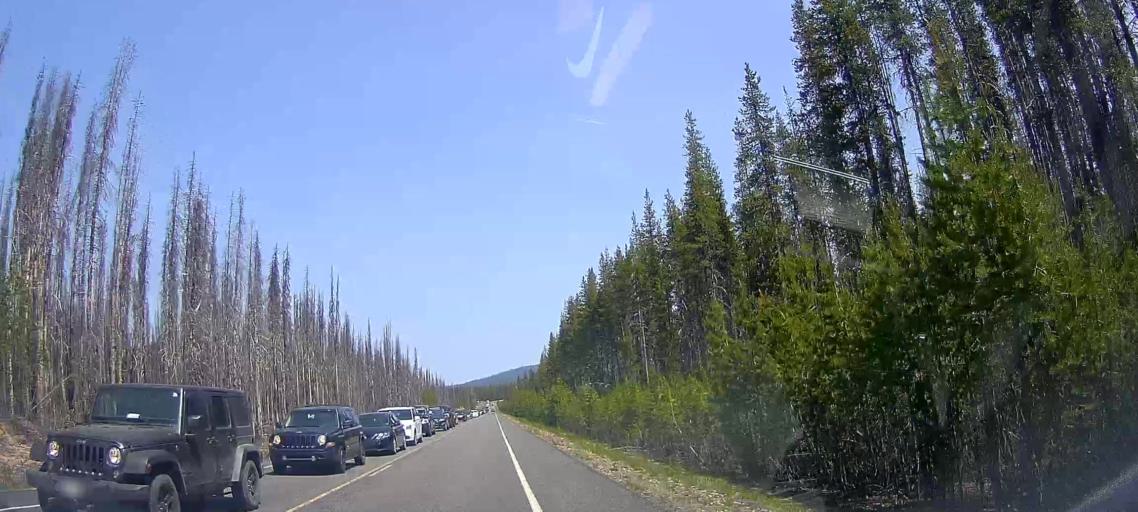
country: US
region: Oregon
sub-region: Lane County
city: Oakridge
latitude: 43.0786
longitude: -122.1178
